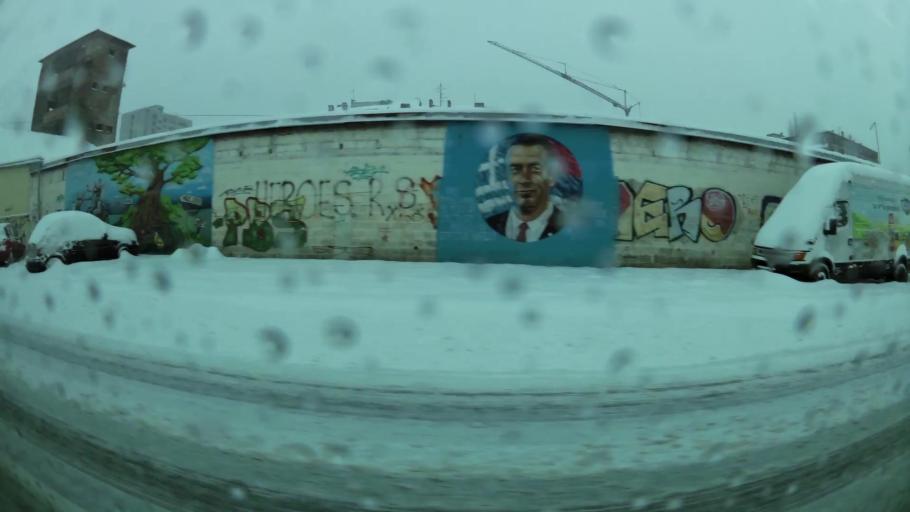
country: RS
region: Central Serbia
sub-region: Belgrade
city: Stari Grad
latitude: 44.8284
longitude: 20.4592
